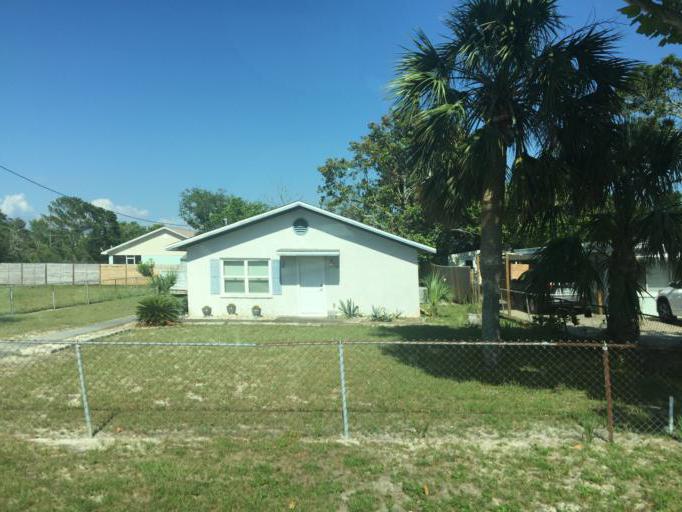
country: US
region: Florida
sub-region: Bay County
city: Panama City Beach
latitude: 30.2030
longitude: -85.8438
